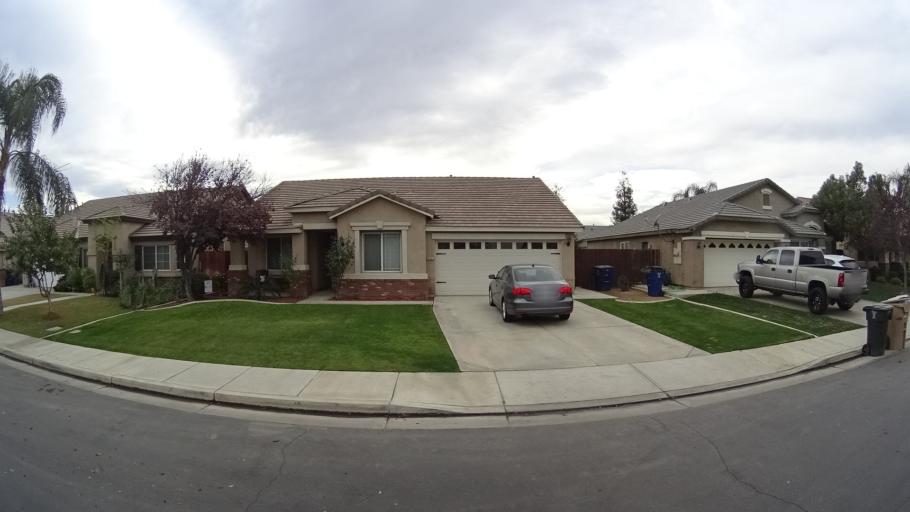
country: US
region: California
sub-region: Kern County
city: Rosedale
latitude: 35.4069
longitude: -119.1490
